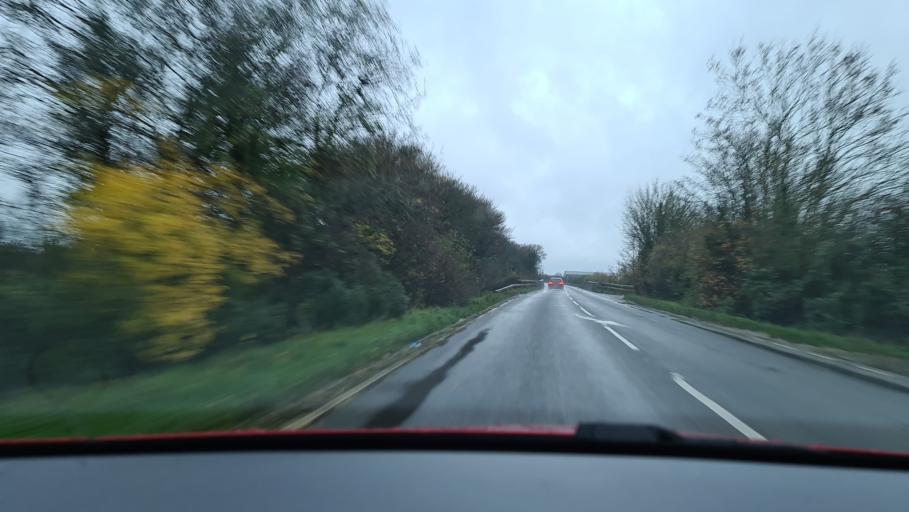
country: GB
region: England
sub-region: Oxfordshire
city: Somerton
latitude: 51.9374
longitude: -1.2139
